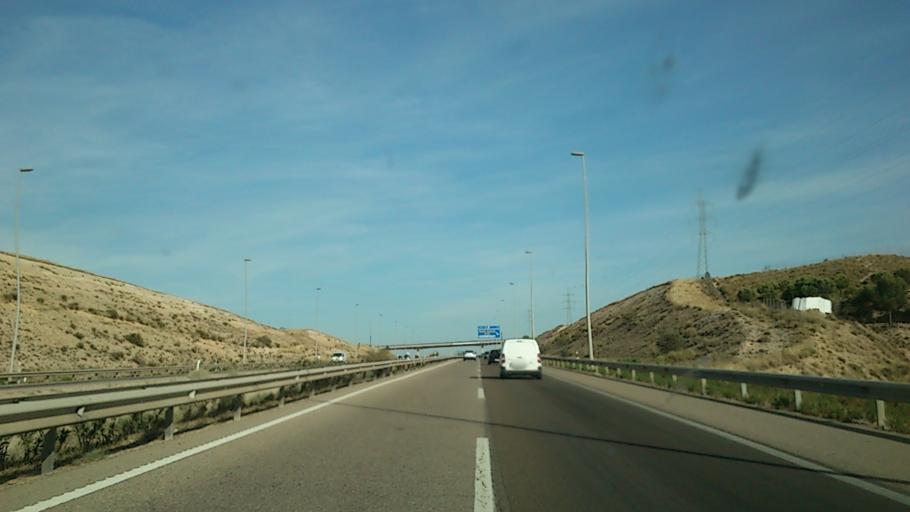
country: ES
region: Aragon
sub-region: Provincia de Zaragoza
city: Cuarte de Huerva
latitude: 41.6069
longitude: -0.9080
